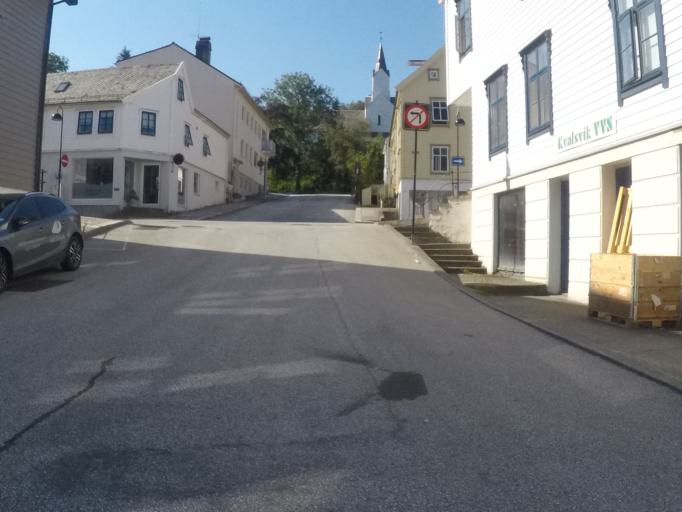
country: NO
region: Sogn og Fjordane
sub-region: Flora
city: Floro
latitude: 61.6002
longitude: 5.0293
